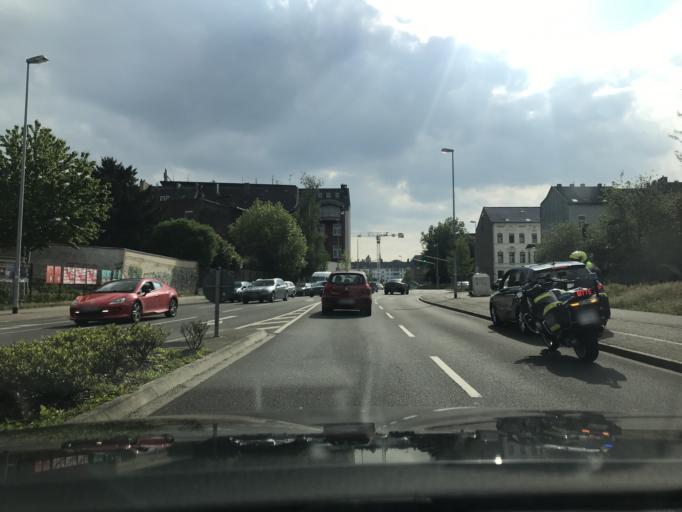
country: DE
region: North Rhine-Westphalia
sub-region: Regierungsbezirk Dusseldorf
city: Monchengladbach
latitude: 51.1991
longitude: 6.4459
